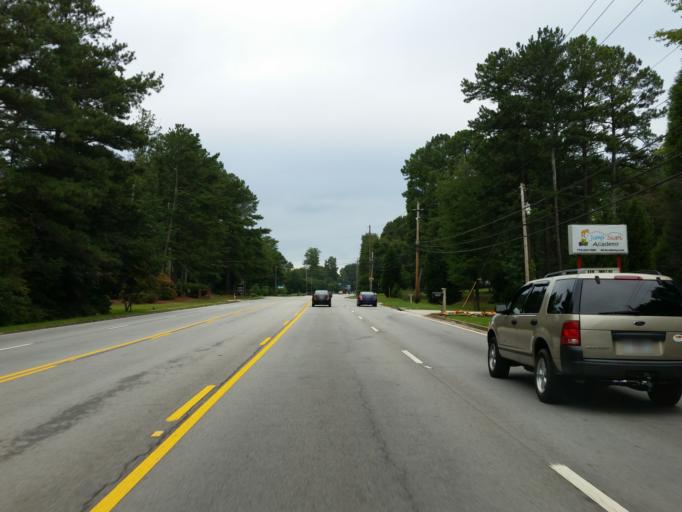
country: US
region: Georgia
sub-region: Cobb County
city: Powder Springs
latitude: 33.8743
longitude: -84.6245
